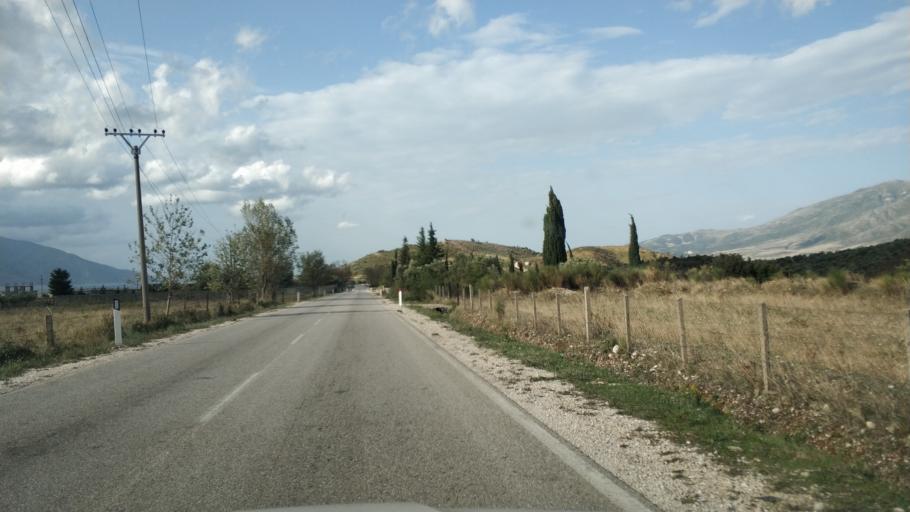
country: AL
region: Vlore
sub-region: Rrethi i Vlores
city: Orikum
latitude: 40.2902
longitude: 19.4926
